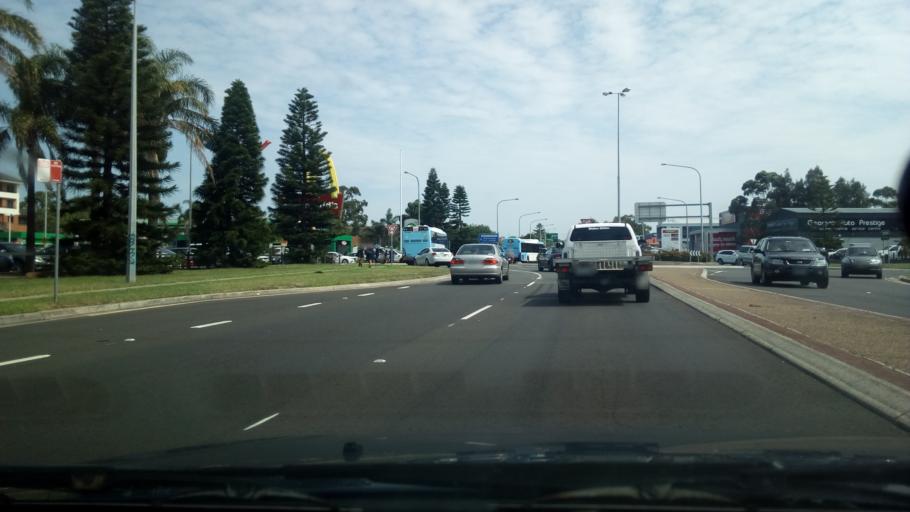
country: AU
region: New South Wales
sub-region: Wollongong
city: Fairy Meadow
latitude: -34.4025
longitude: 150.8914
